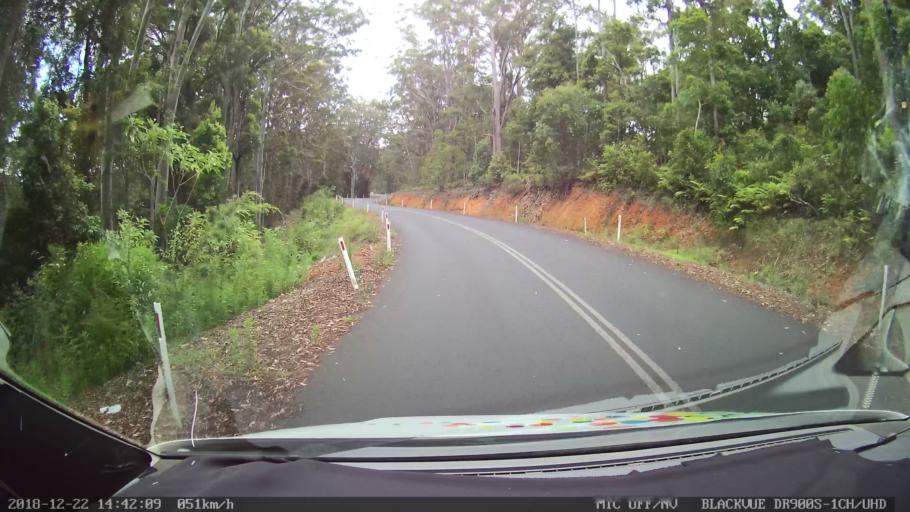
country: AU
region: New South Wales
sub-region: Bellingen
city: Dorrigo
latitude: -30.1573
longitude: 152.5853
